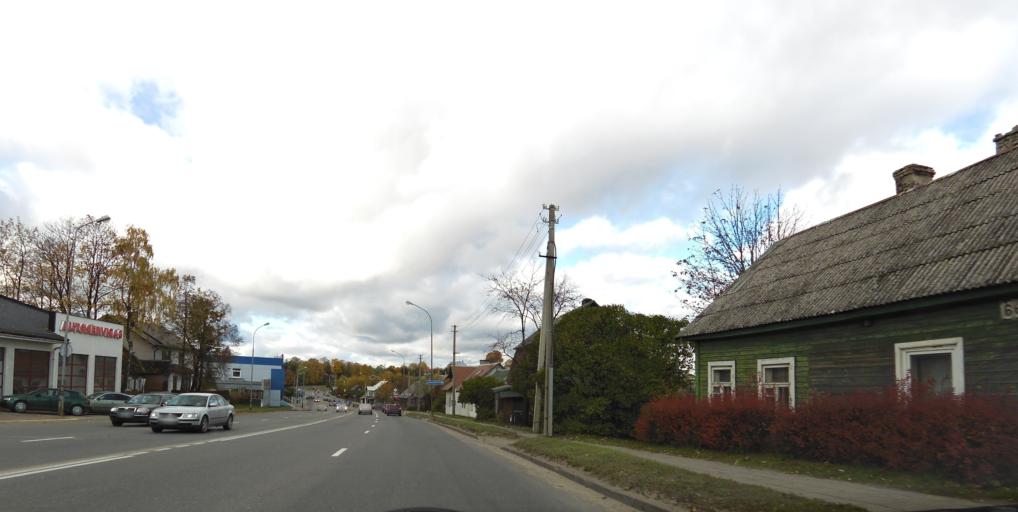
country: LT
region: Vilnius County
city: Rasos
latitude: 54.6610
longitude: 25.3030
